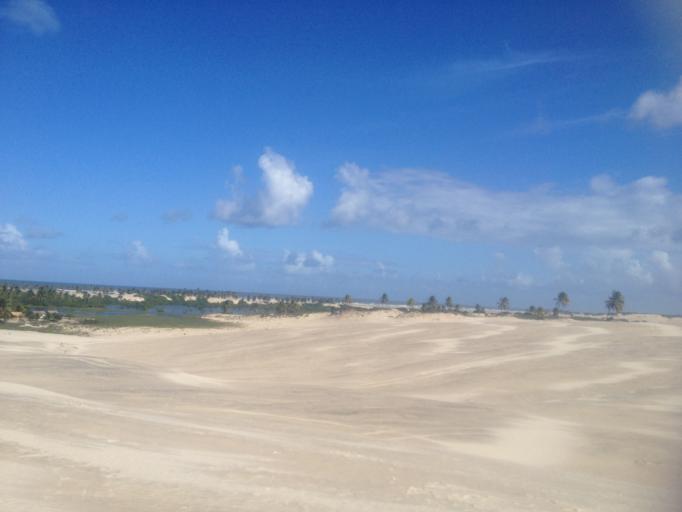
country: BR
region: Sergipe
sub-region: Indiaroba
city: Indiaroba
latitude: -11.4652
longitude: -37.3667
